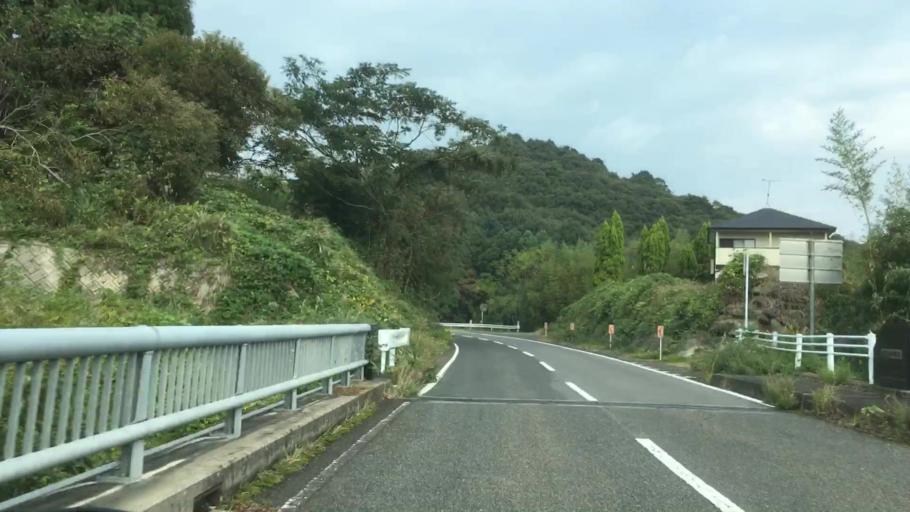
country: JP
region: Nagasaki
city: Sasebo
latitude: 32.9951
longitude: 129.7211
